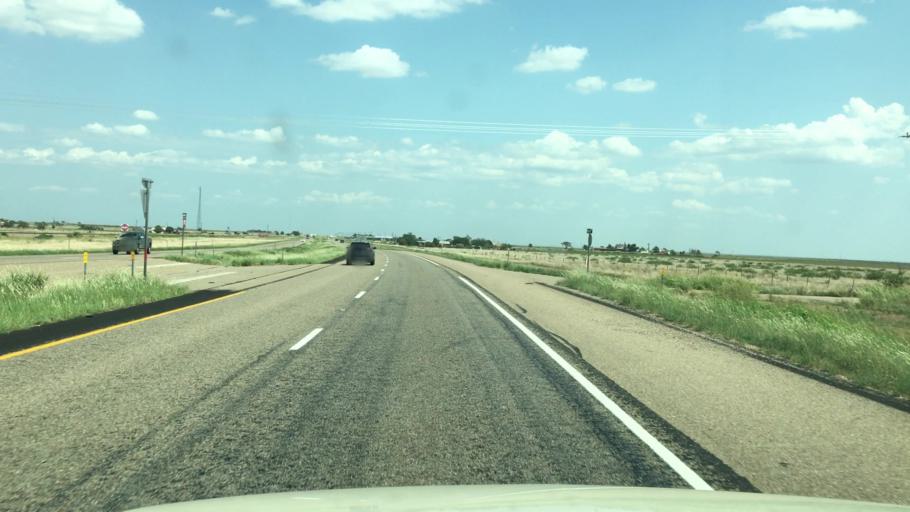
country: US
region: Texas
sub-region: Armstrong County
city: Claude
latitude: 35.0345
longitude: -101.1953
